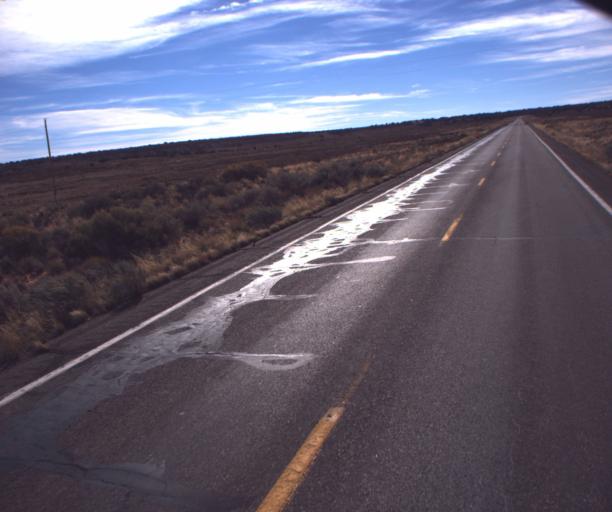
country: US
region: Arizona
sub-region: Coconino County
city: Kaibito
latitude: 36.6942
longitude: -111.2616
